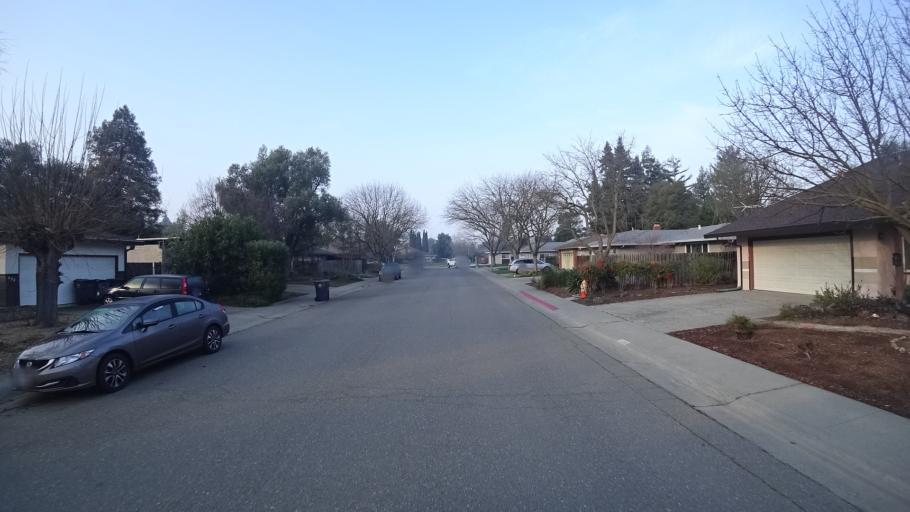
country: US
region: California
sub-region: Yolo County
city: Davis
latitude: 38.5646
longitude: -121.7474
